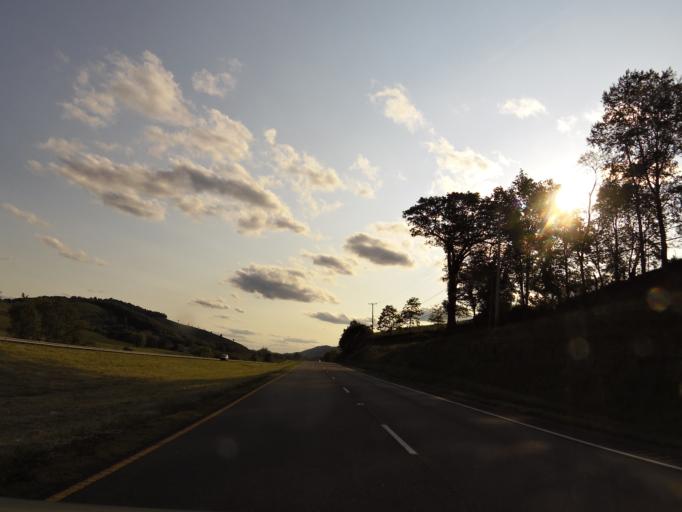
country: US
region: Virginia
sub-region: Russell County
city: Honaker
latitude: 36.9720
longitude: -81.8981
